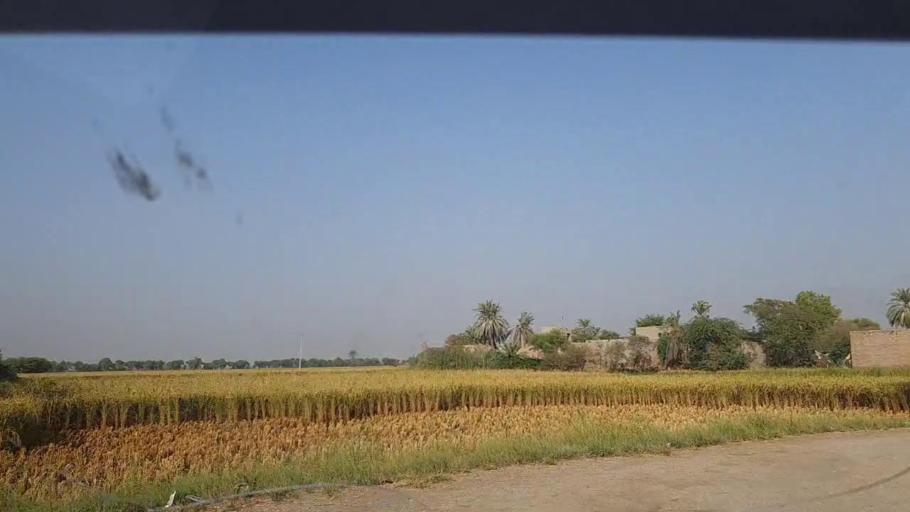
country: PK
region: Sindh
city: Shikarpur
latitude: 28.1172
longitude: 68.5816
